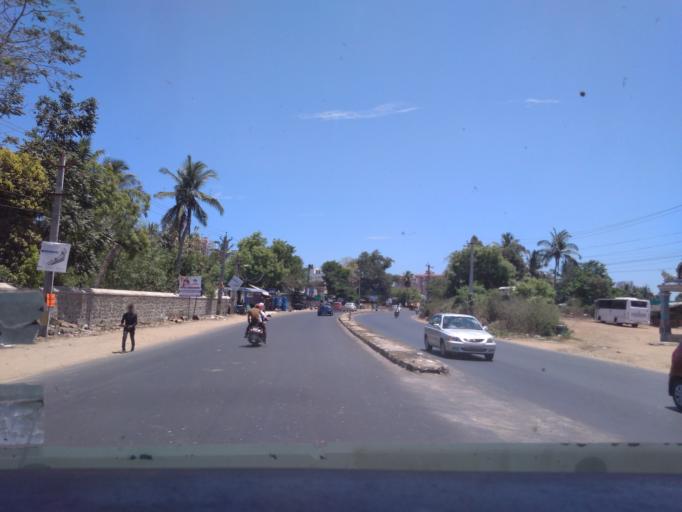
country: IN
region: Tamil Nadu
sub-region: Kancheepuram
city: Injambakkam
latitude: 12.8278
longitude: 80.2309
